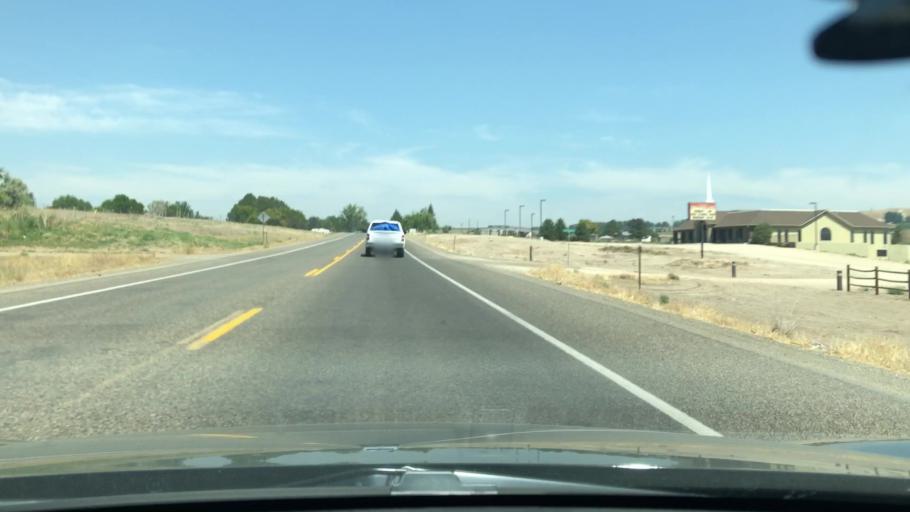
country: US
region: Idaho
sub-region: Owyhee County
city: Homedale
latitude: 43.6239
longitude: -116.9161
